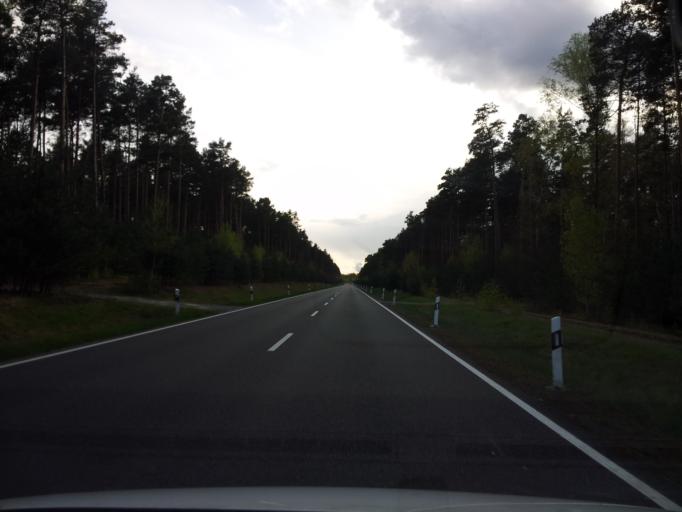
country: DE
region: Brandenburg
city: Janschwalde
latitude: 51.8826
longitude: 14.5625
